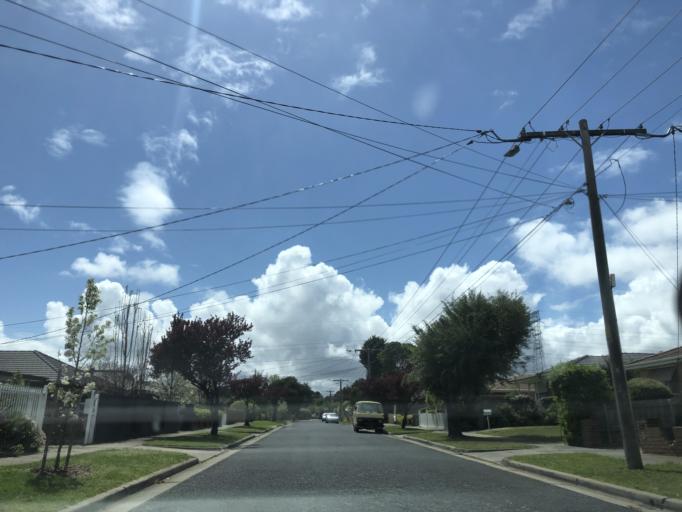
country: AU
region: Victoria
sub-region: Monash
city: Oakleigh South
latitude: -37.9382
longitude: 145.0857
